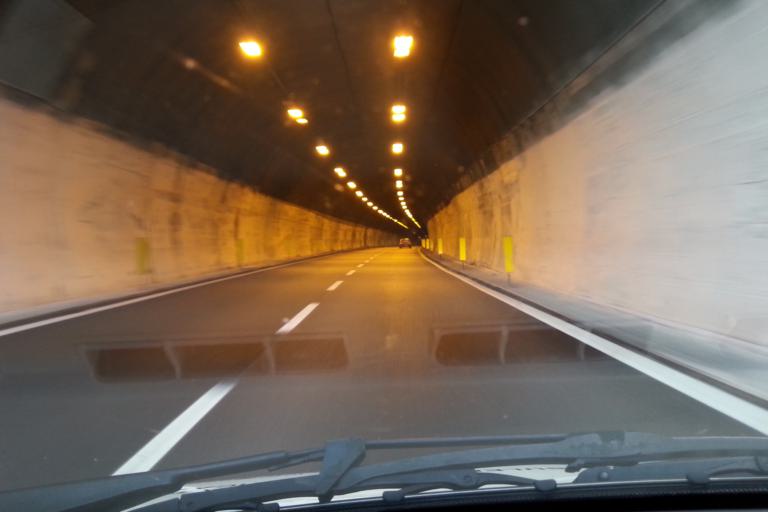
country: IT
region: Liguria
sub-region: Provincia di Savona
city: Feglino
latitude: 44.2106
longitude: 8.3190
